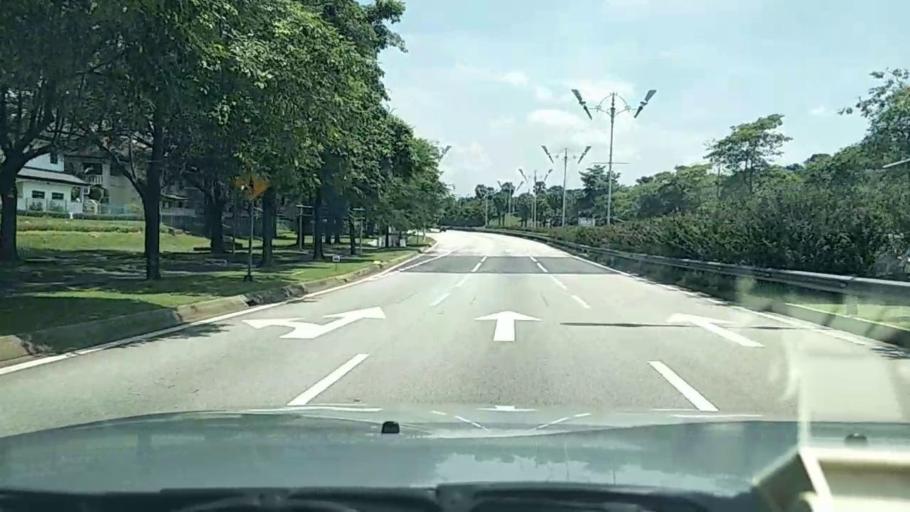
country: MY
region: Putrajaya
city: Putrajaya
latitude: 2.9546
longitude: 101.6858
